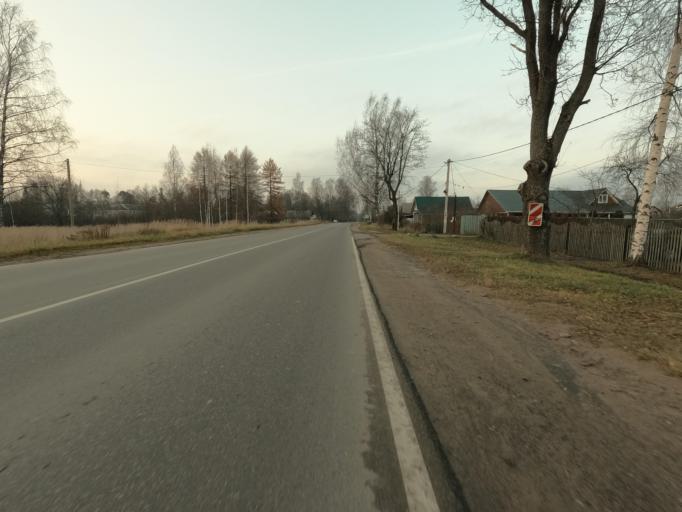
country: RU
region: Leningrad
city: Kirovsk
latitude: 59.8311
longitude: 30.9888
